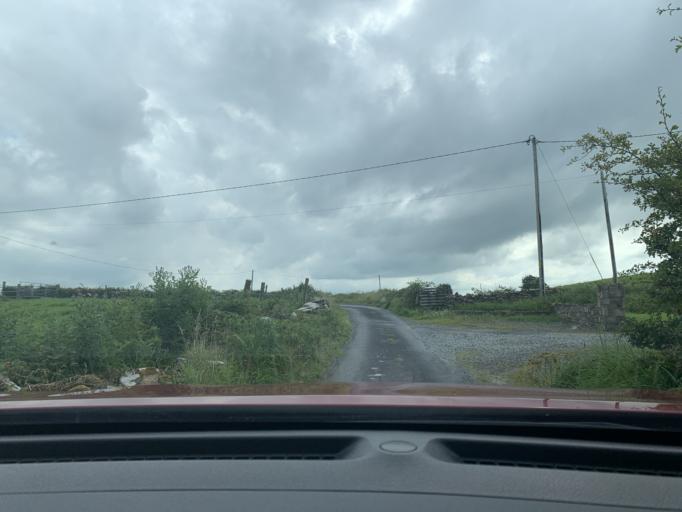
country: IE
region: Connaught
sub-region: Maigh Eo
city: Kiltamagh
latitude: 53.8416
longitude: -9.0036
